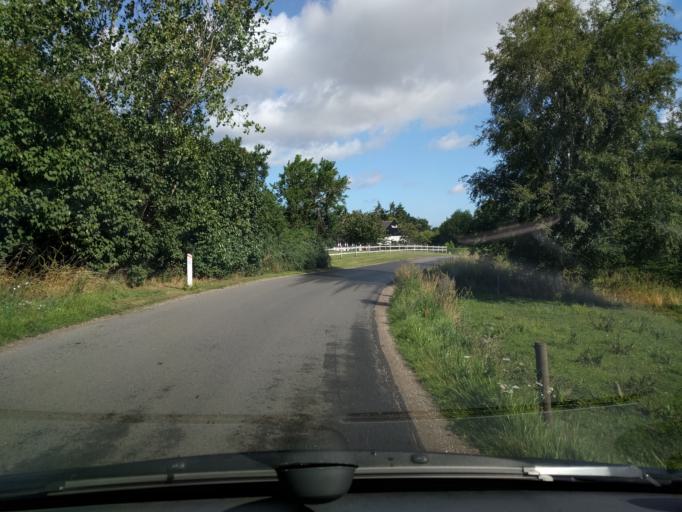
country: DK
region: South Denmark
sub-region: Kerteminde Kommune
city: Langeskov
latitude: 55.3669
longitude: 10.5872
